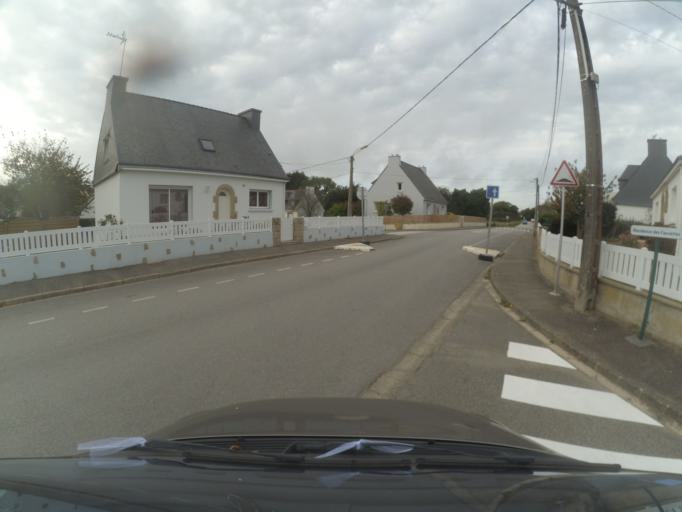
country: FR
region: Brittany
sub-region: Departement du Morbihan
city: Guidel-Plage
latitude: 47.7897
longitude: -3.4922
